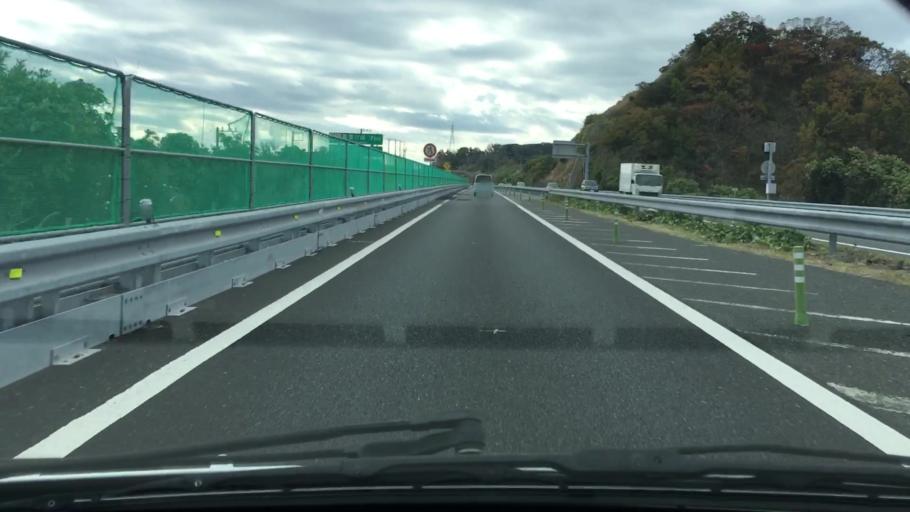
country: JP
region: Chiba
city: Kimitsu
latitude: 35.2456
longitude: 139.8900
